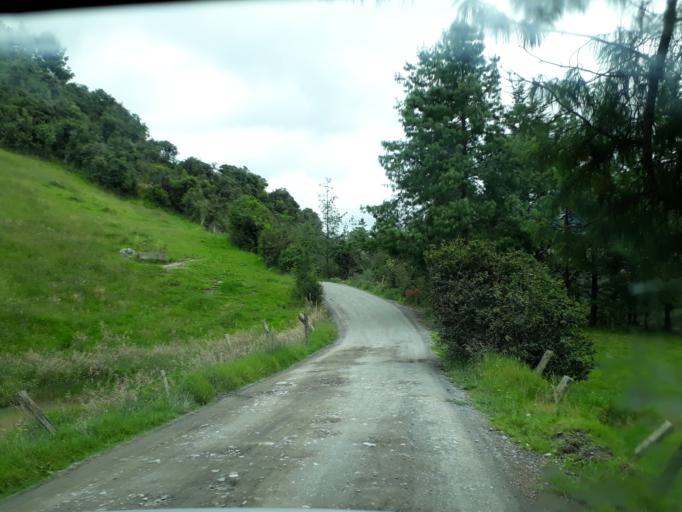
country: CO
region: Cundinamarca
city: Carmen de Carupa
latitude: 5.3137
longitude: -73.8951
